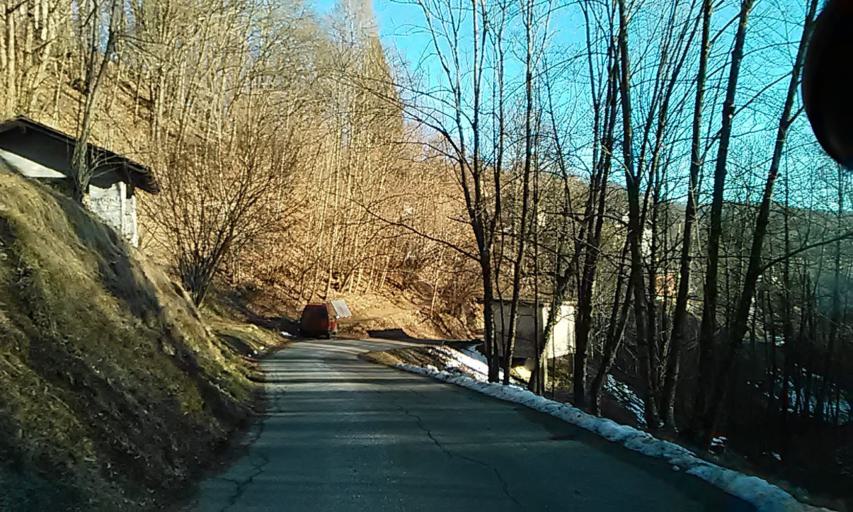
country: IT
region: Piedmont
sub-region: Provincia di Vercelli
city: Cellio
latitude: 45.7637
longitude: 8.3342
